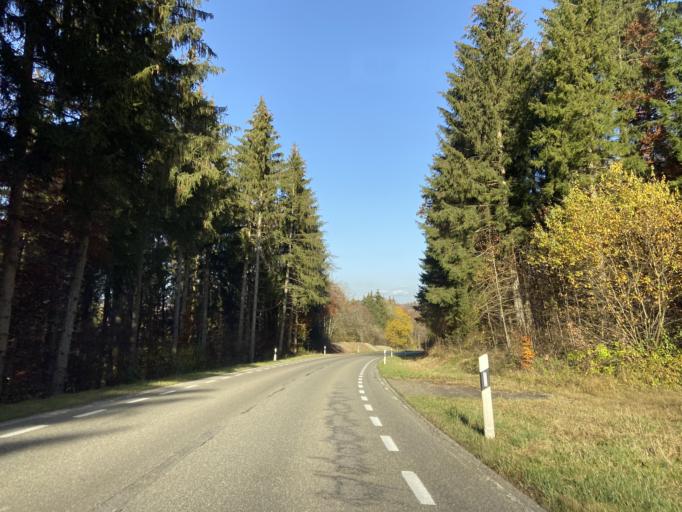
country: DE
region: Baden-Wuerttemberg
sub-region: Tuebingen Region
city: Sigmaringendorf
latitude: 48.0586
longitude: 9.2599
